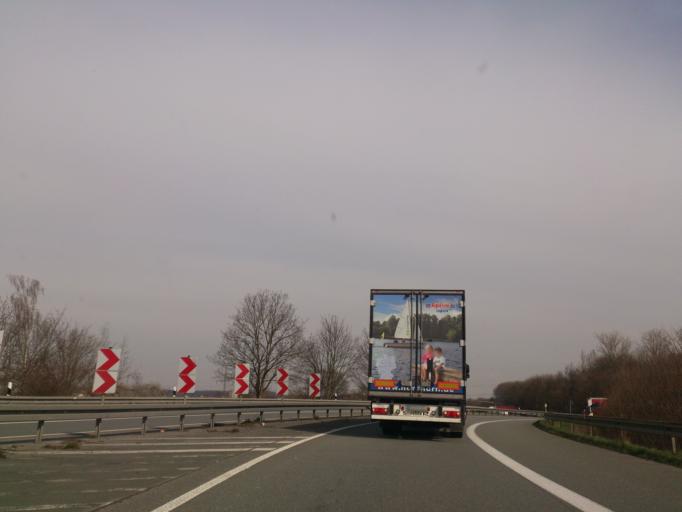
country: DE
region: North Rhine-Westphalia
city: Erwitte
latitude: 51.6055
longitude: 8.3102
